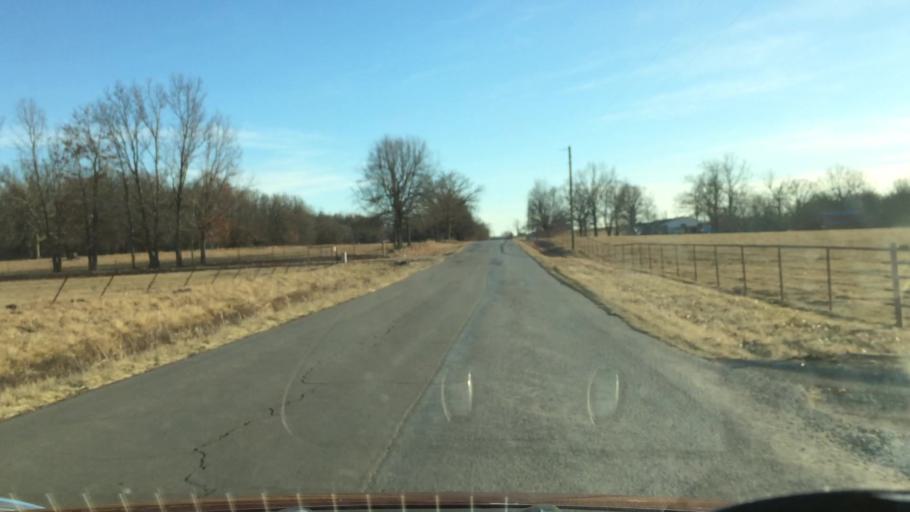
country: US
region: Missouri
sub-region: Webster County
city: Marshfield
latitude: 37.3320
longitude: -92.9840
